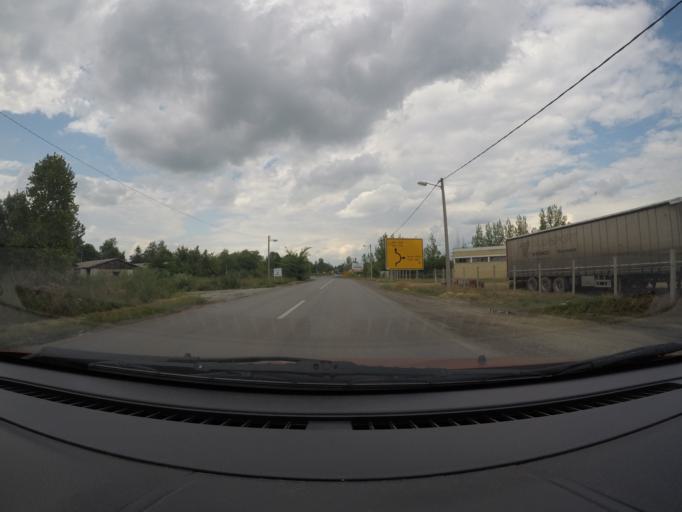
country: RS
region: Autonomna Pokrajina Vojvodina
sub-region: Srednjebanatski Okrug
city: Zitiste
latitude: 45.4779
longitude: 20.5511
